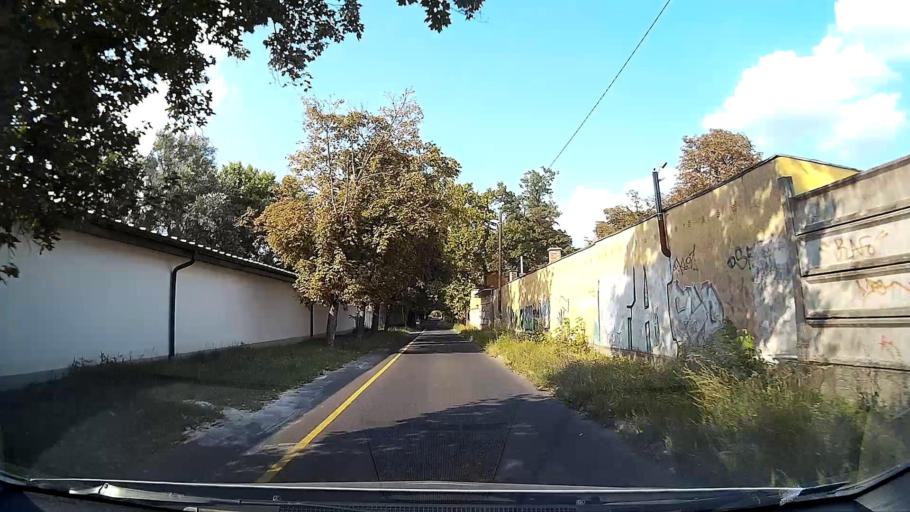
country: HU
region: Budapest
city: Budapest III. keruelet
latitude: 47.5624
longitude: 19.0503
